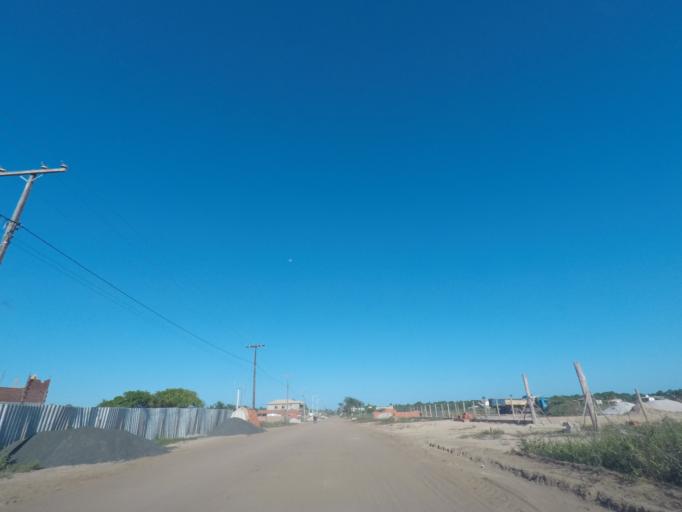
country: BR
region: Bahia
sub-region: Camamu
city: Camamu
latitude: -13.9322
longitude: -38.9416
